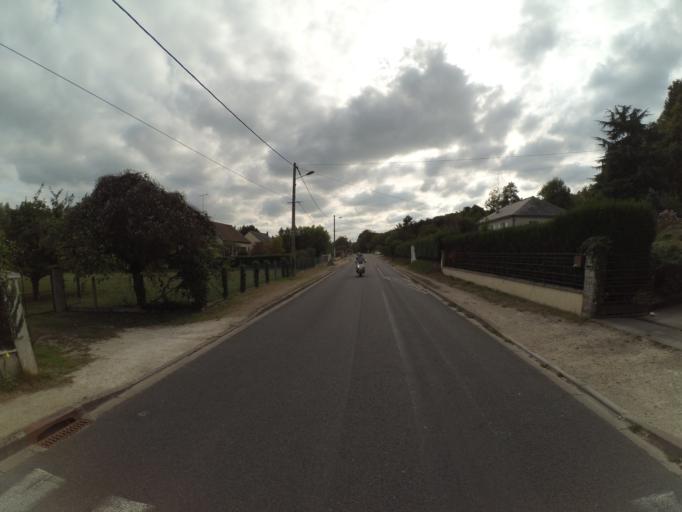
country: FR
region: Centre
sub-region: Departement d'Indre-et-Loire
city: Reugny
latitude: 47.4766
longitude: 0.8815
